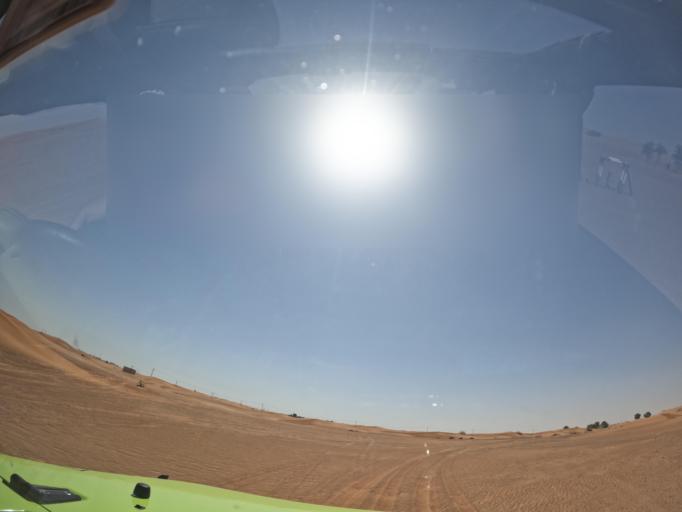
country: AE
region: Ash Shariqah
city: Adh Dhayd
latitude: 25.0109
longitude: 55.7386
